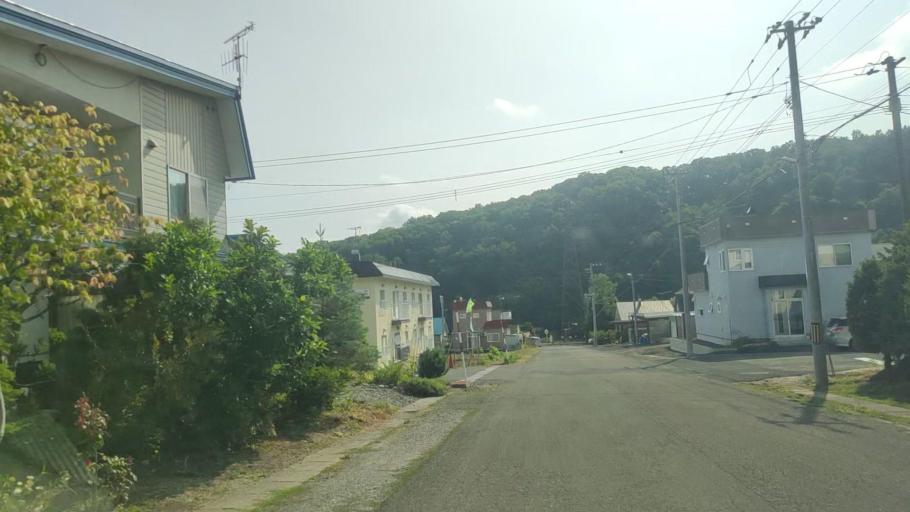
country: JP
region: Hokkaido
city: Shimo-furano
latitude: 43.3422
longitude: 142.3686
